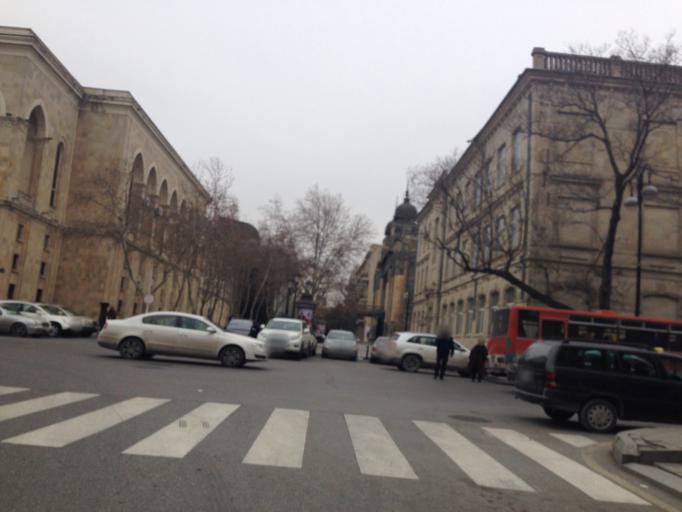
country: AZ
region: Baki
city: Baku
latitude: 40.3749
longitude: 49.8466
